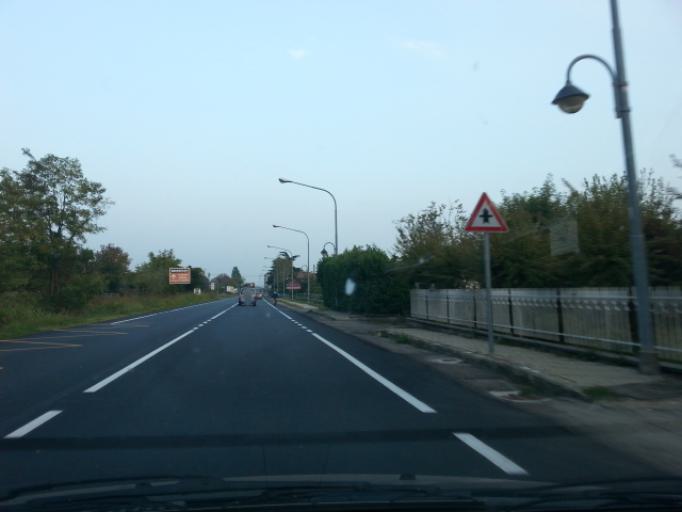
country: IT
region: Piedmont
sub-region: Provincia di Torino
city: Sangano
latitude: 45.0293
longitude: 7.4445
